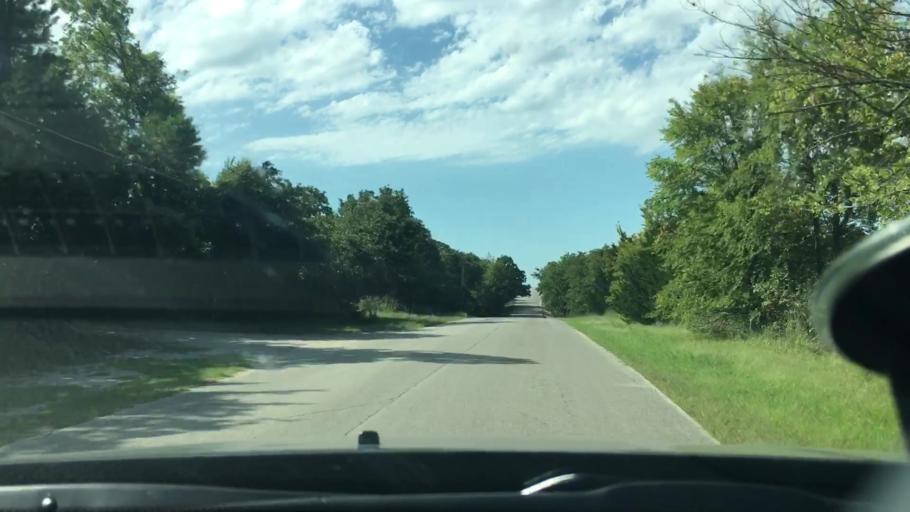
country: US
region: Oklahoma
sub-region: Carter County
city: Ardmore
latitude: 34.1468
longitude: -97.0906
